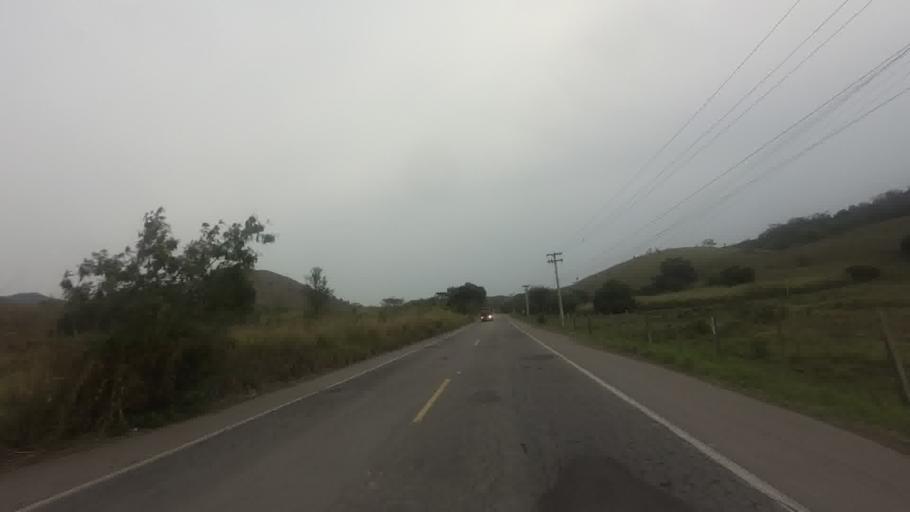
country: BR
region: Rio de Janeiro
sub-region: Santo Antonio De Padua
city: Santo Antonio de Padua
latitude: -21.5901
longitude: -42.2229
